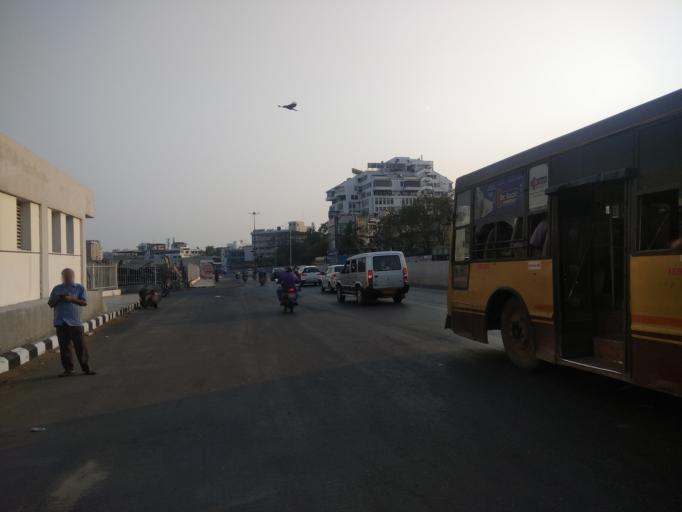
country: IN
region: Tamil Nadu
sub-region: Kancheepuram
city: Alandur
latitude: 13.0211
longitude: 80.2257
